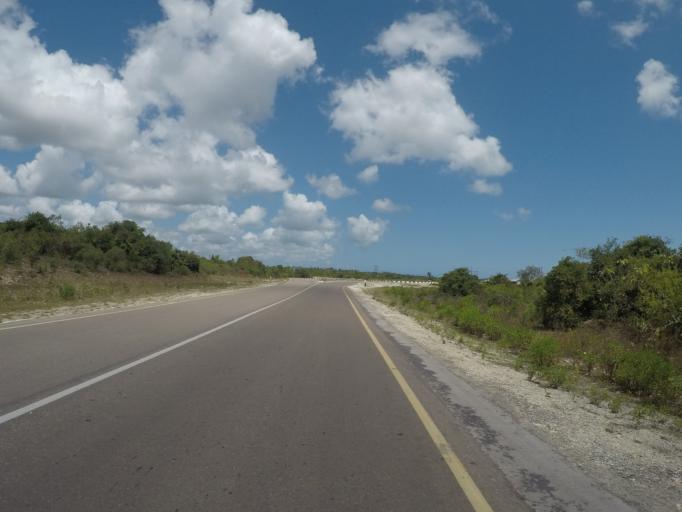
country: TZ
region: Zanzibar Central/South
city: Koani
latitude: -6.2762
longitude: 39.3651
